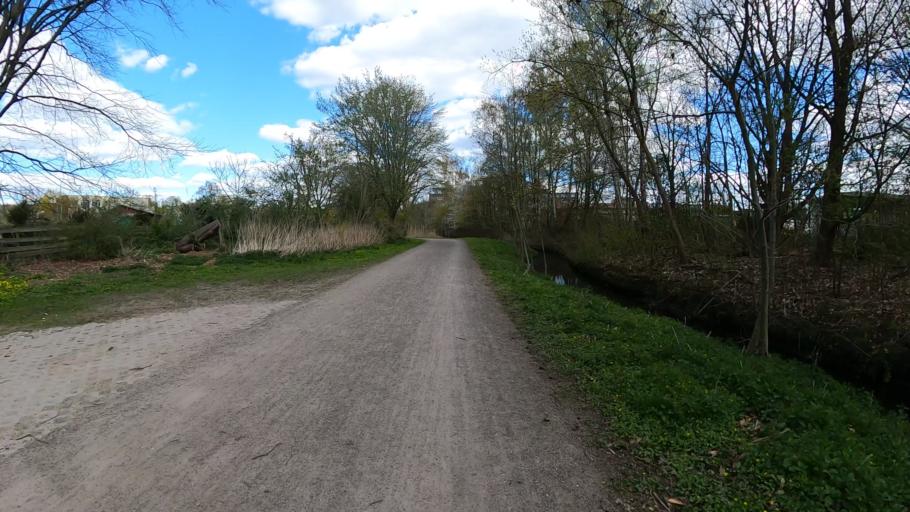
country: DE
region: Hamburg
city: Bergedorf
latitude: 53.4900
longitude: 10.1931
